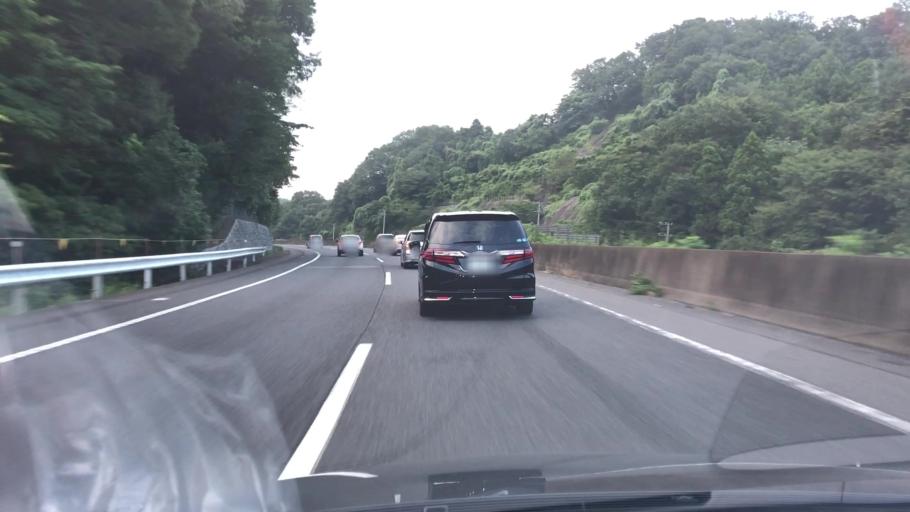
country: JP
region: Tokyo
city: Hachioji
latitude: 35.6445
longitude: 139.2653
